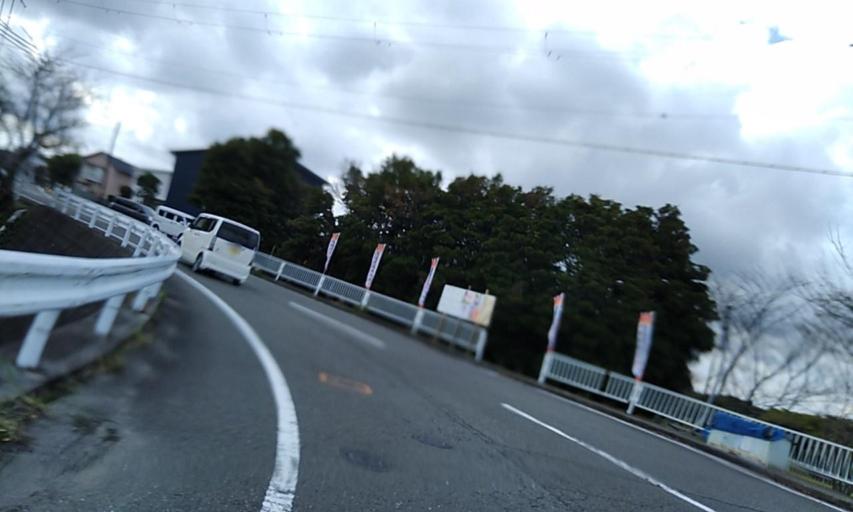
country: JP
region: Wakayama
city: Shingu
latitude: 33.5877
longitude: 135.9491
